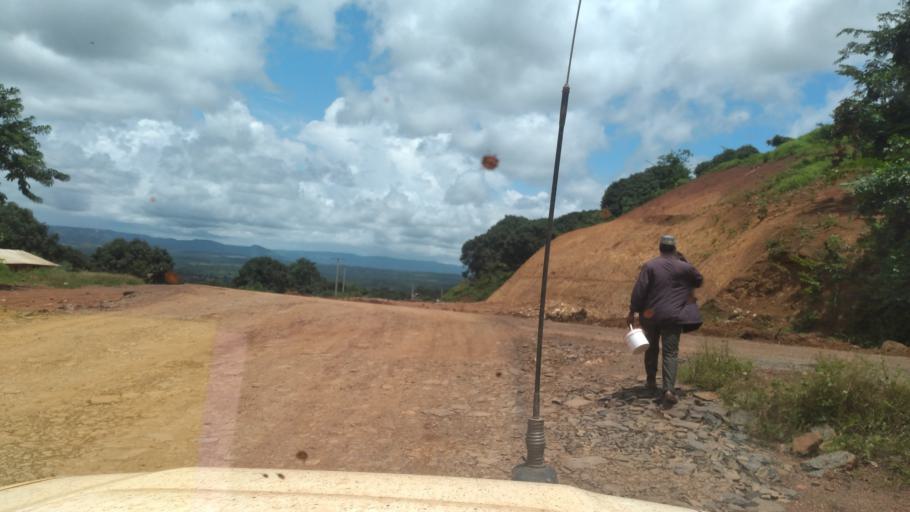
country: GN
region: Kindia
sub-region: Kindia
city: Kindia
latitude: 10.1780
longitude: -12.4786
